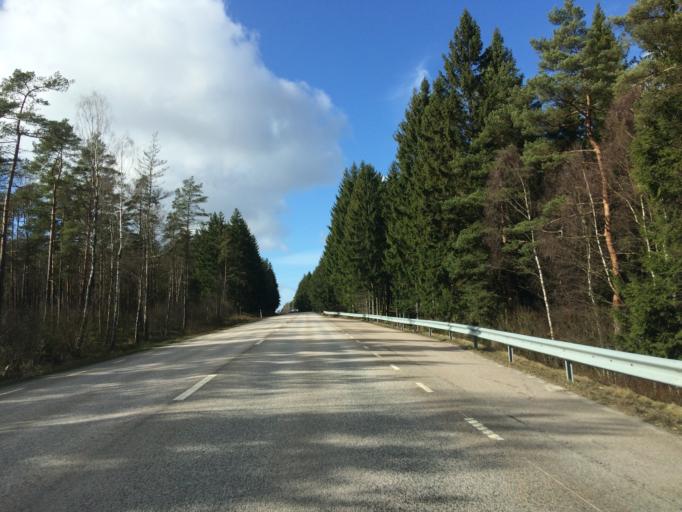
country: SE
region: Halland
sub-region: Laholms Kommun
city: Knared
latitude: 56.4909
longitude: 13.4053
